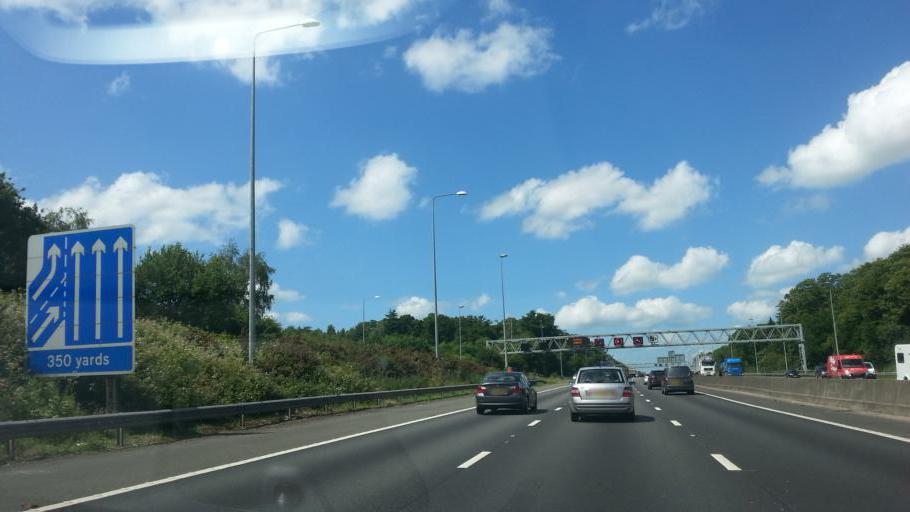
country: GB
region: England
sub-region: Buckinghamshire
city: Gerrards Cross
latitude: 51.5652
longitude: -0.5334
